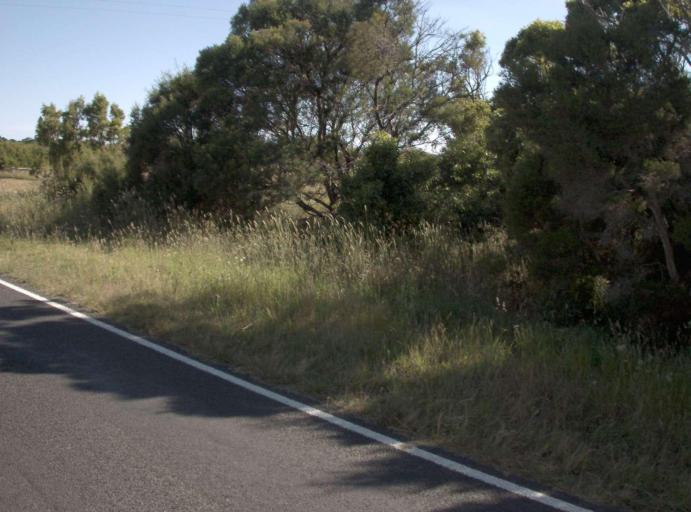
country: AU
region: Victoria
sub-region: Latrobe
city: Traralgon
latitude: -38.6244
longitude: 146.6737
